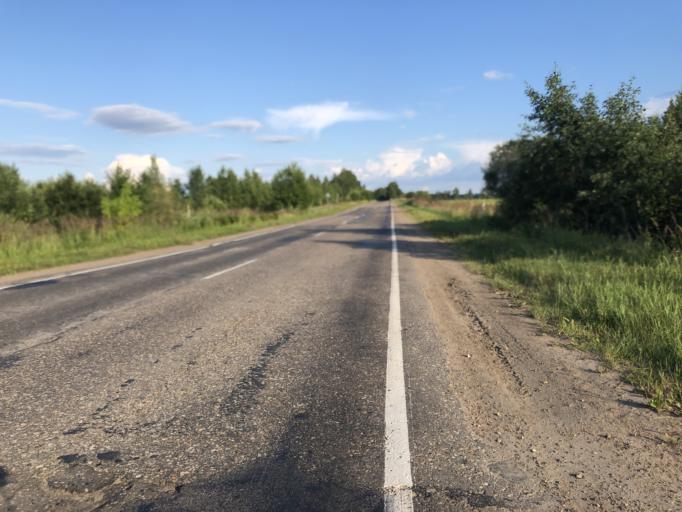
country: RU
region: Tverskaya
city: Rzhev
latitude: 56.2783
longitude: 34.2359
